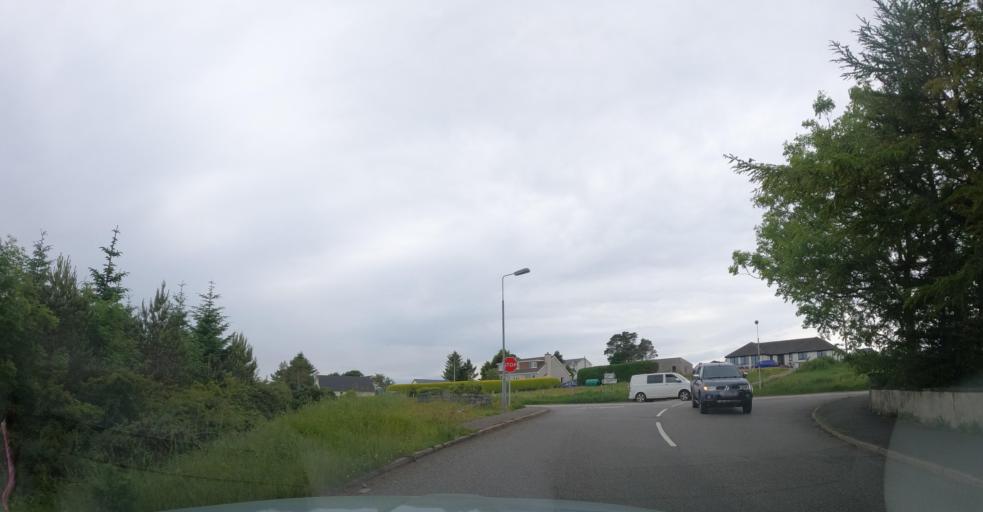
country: GB
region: Scotland
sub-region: Eilean Siar
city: Isle of Lewis
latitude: 58.2336
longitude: -6.3900
